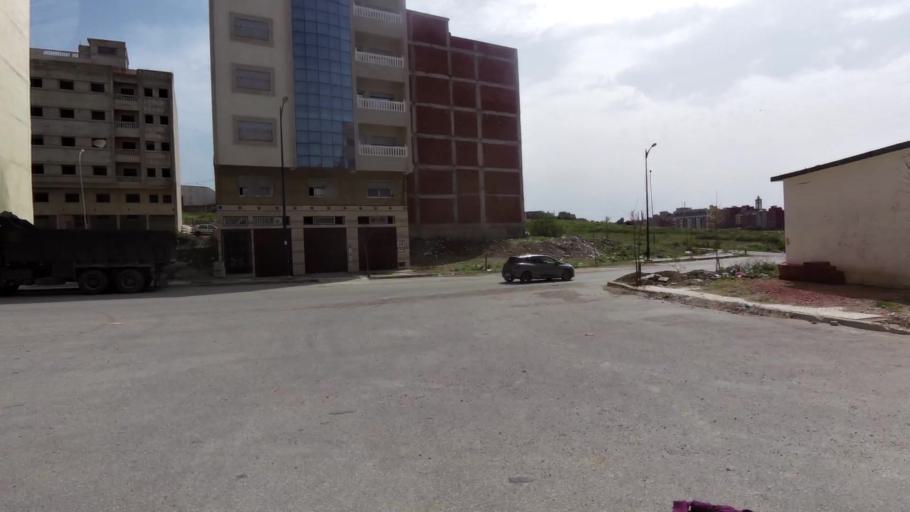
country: MA
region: Tanger-Tetouan
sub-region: Tanger-Assilah
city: Tangier
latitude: 35.7386
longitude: -5.8366
